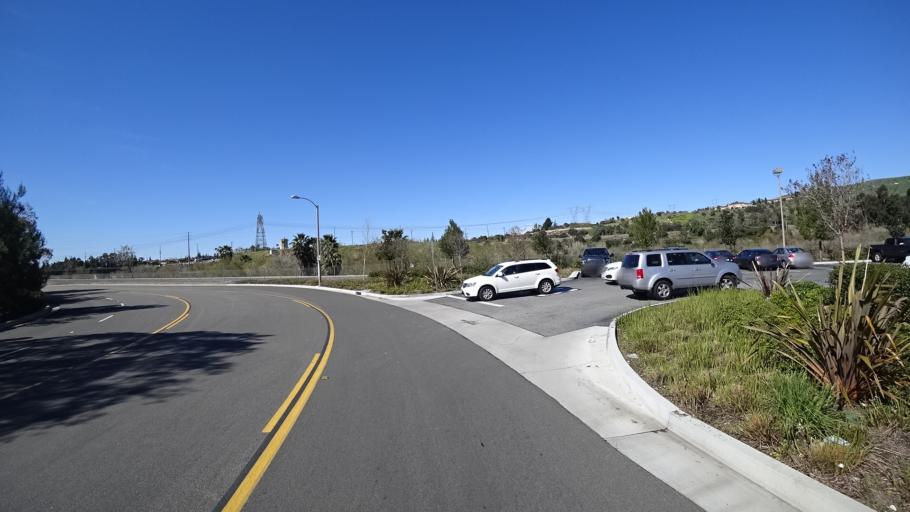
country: US
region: California
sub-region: Orange County
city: Yorba Linda
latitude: 33.8754
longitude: -117.7456
